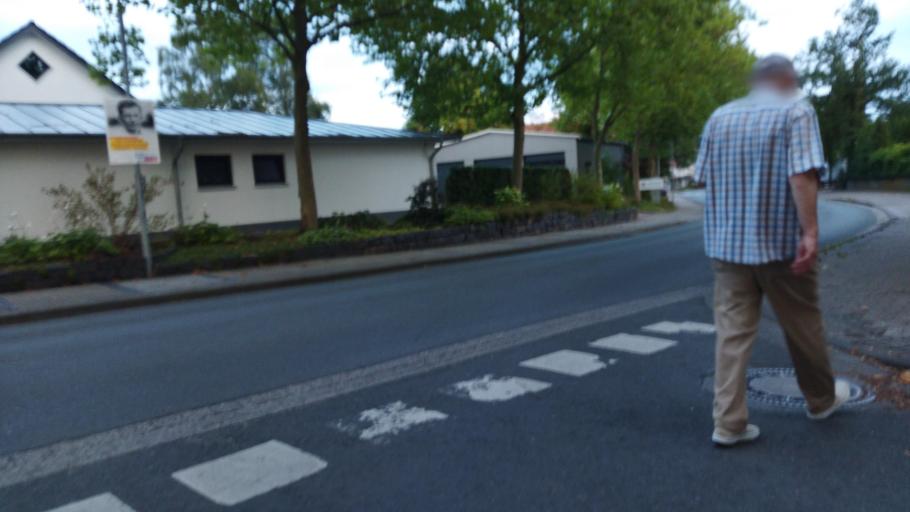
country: DE
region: Lower Saxony
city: Bad Laer
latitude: 52.1049
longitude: 8.0847
